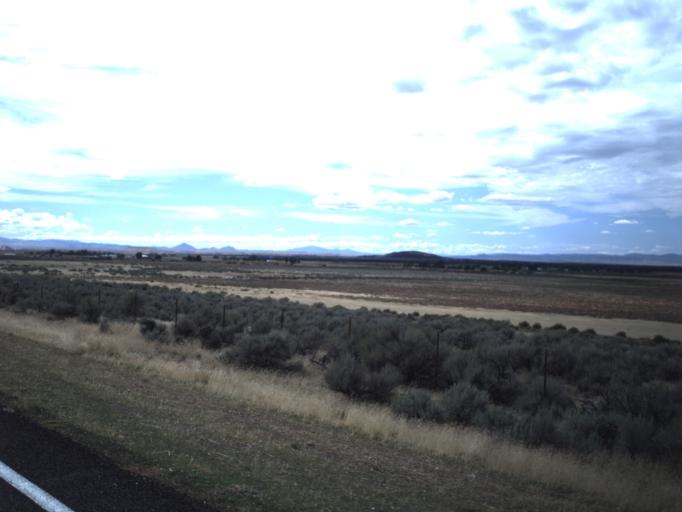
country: US
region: Utah
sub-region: Millard County
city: Fillmore
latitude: 39.0034
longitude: -112.4120
